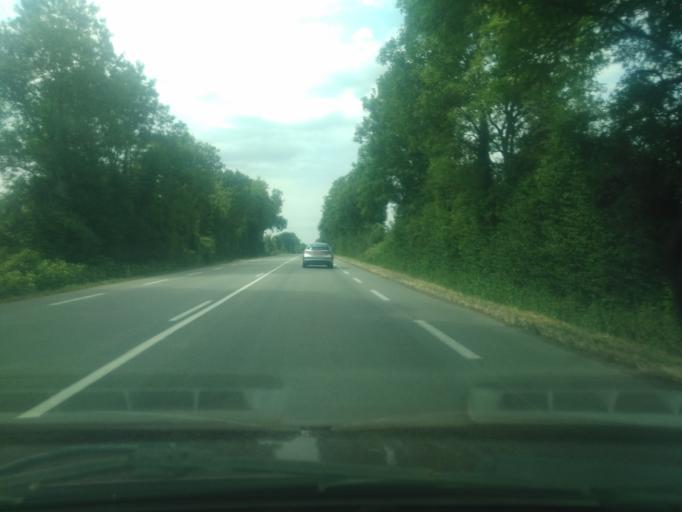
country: FR
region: Pays de la Loire
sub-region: Departement de la Vendee
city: Sainte-Cecile
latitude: 46.7292
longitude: -1.0785
